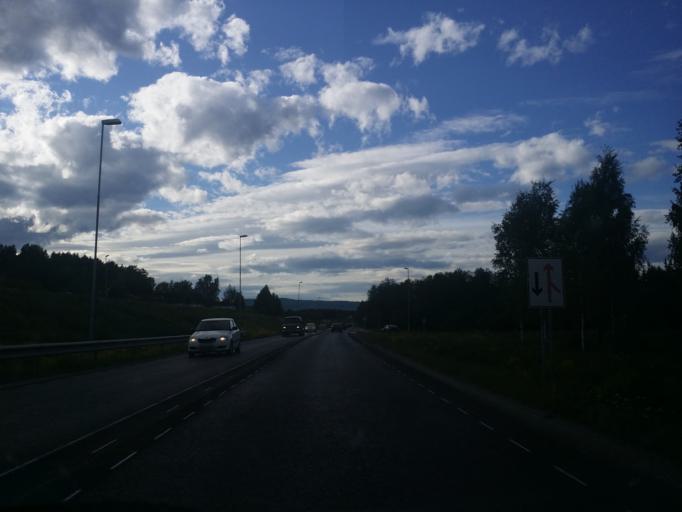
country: NO
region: Hedmark
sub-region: Hamar
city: Hamar
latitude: 60.8148
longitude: 11.0984
